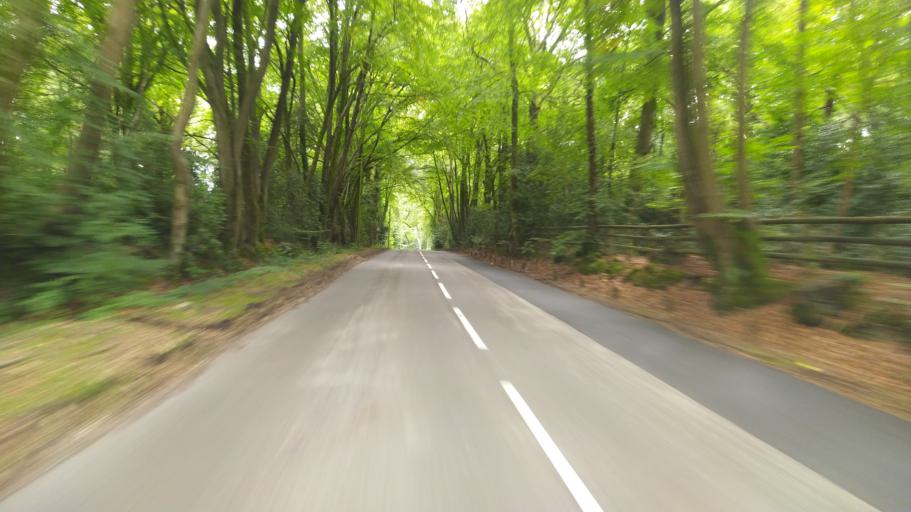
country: GB
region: England
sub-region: Hampshire
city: West Wellow
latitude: 51.0086
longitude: -1.5473
